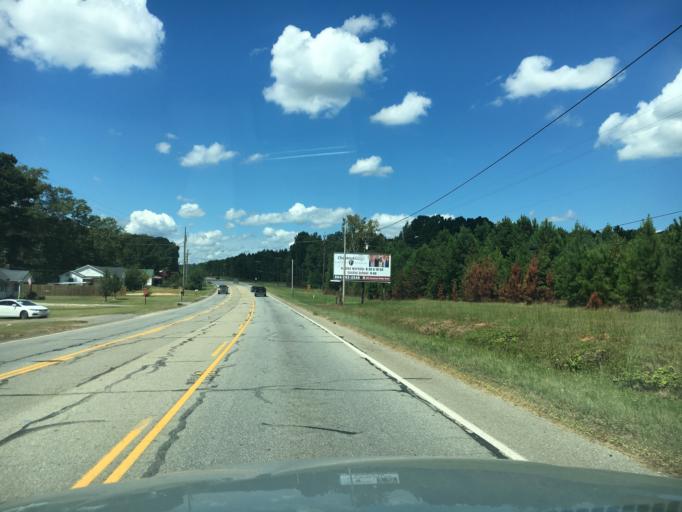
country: US
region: South Carolina
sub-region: Laurens County
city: Laurens
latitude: 34.5007
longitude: -82.0521
